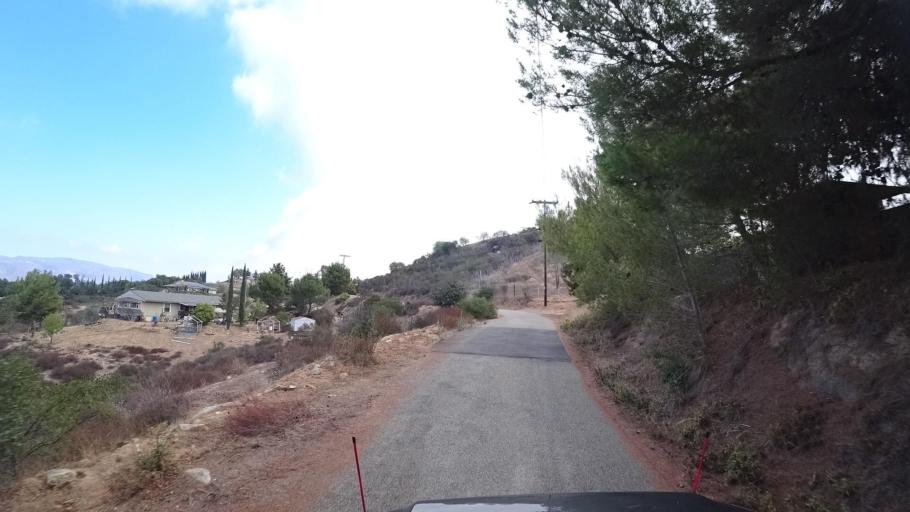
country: US
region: California
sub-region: San Diego County
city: Fallbrook
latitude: 33.4260
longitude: -117.3126
